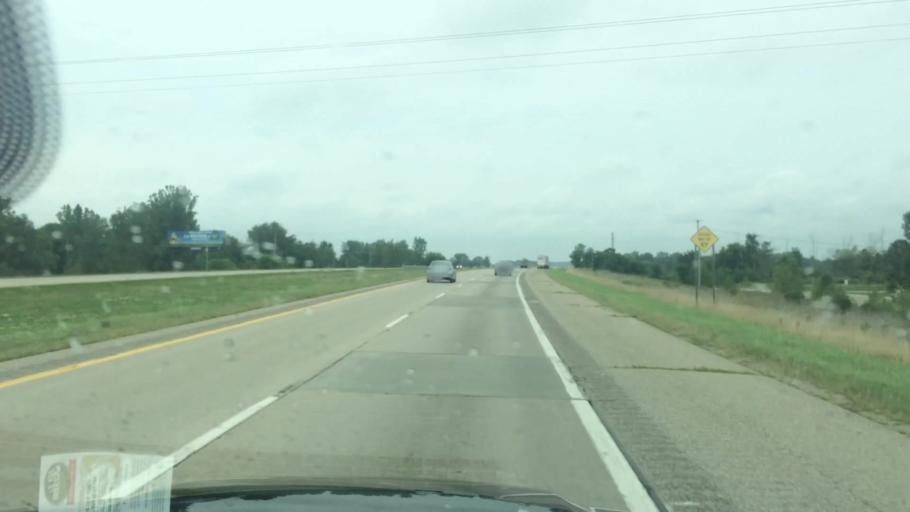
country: US
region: Michigan
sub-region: Eaton County
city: Potterville
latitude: 42.6044
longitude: -84.7717
